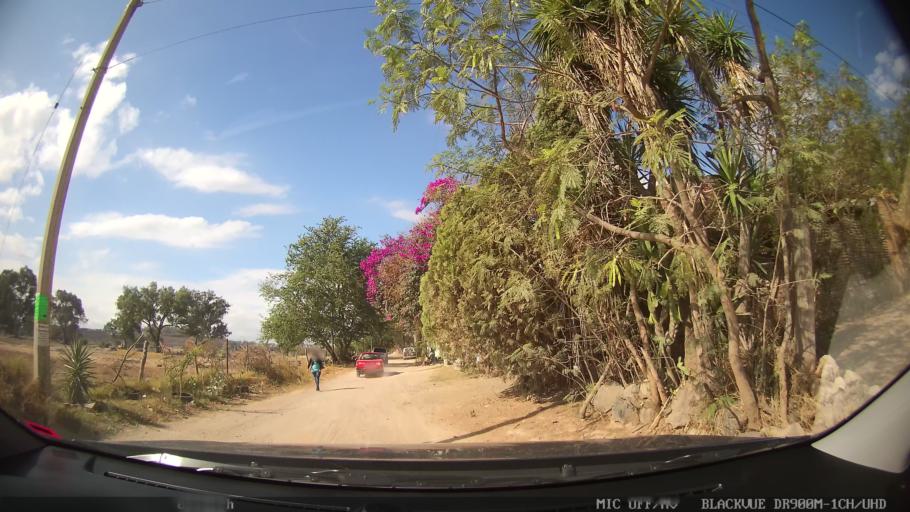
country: MX
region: Jalisco
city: Tonala
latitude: 20.6502
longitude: -103.2476
